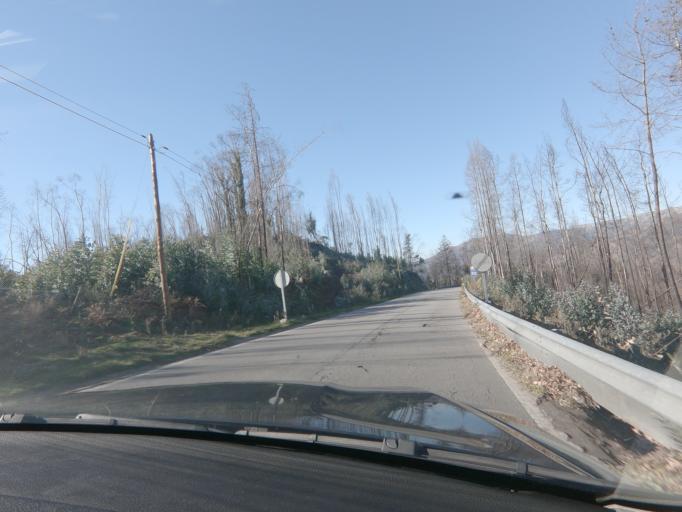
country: PT
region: Viseu
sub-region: Oliveira de Frades
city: Oliveira de Frades
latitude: 40.7312
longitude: -8.1482
